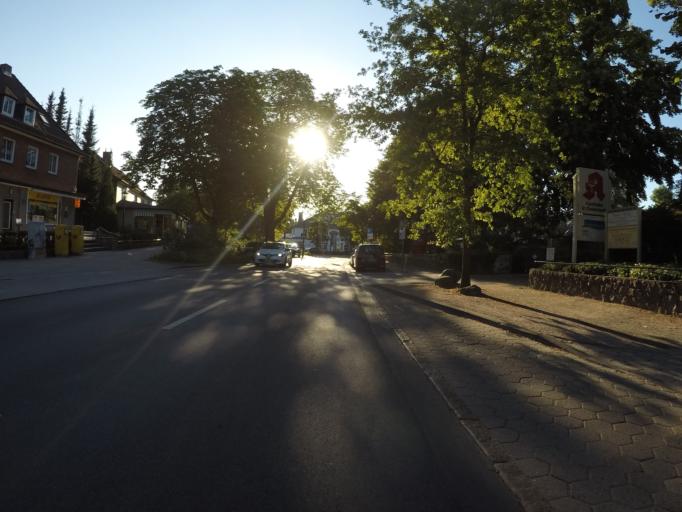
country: DE
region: Hamburg
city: Duvenstedt
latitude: 53.7076
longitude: 10.1095
